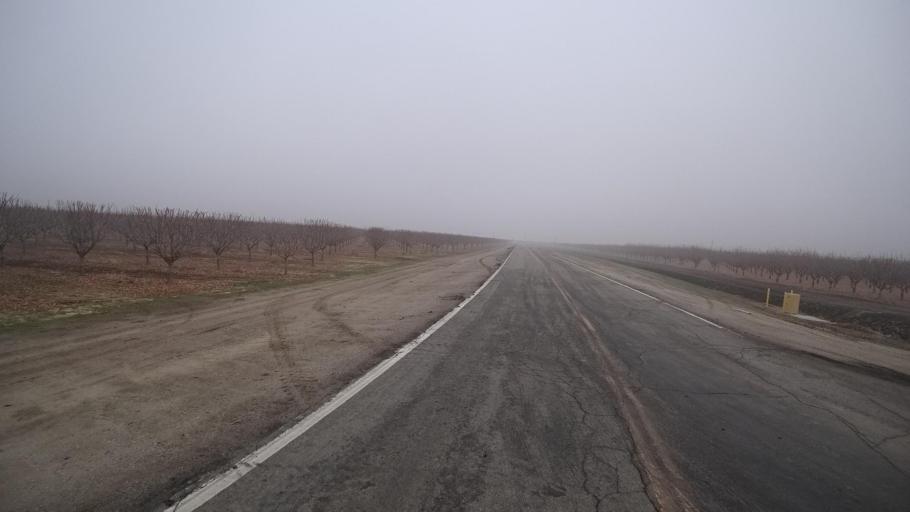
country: US
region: California
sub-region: Kern County
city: Buttonwillow
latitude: 35.4285
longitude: -119.5411
